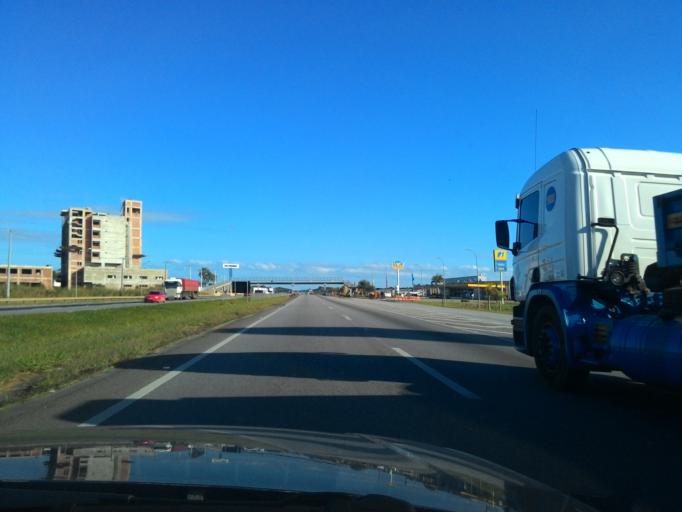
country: BR
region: Sao Paulo
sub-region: Registro
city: Registro
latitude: -24.5275
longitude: -47.8558
